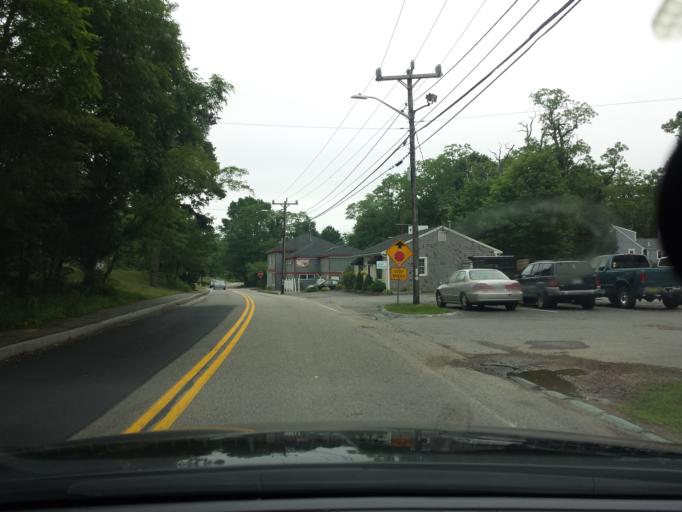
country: US
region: Massachusetts
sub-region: Barnstable County
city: Marstons Mills
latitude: 41.6543
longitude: -70.4129
